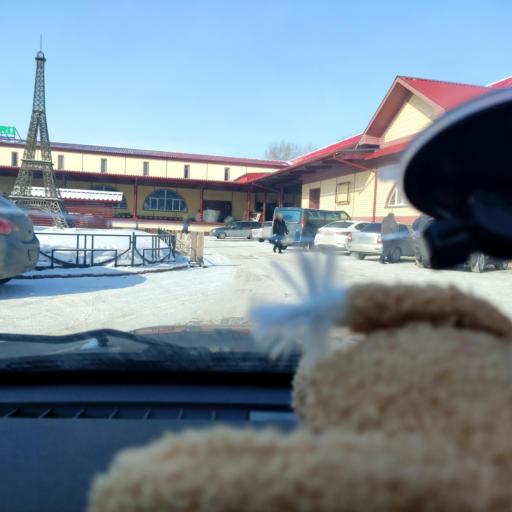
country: RU
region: Samara
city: Tol'yatti
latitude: 53.5618
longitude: 49.3070
